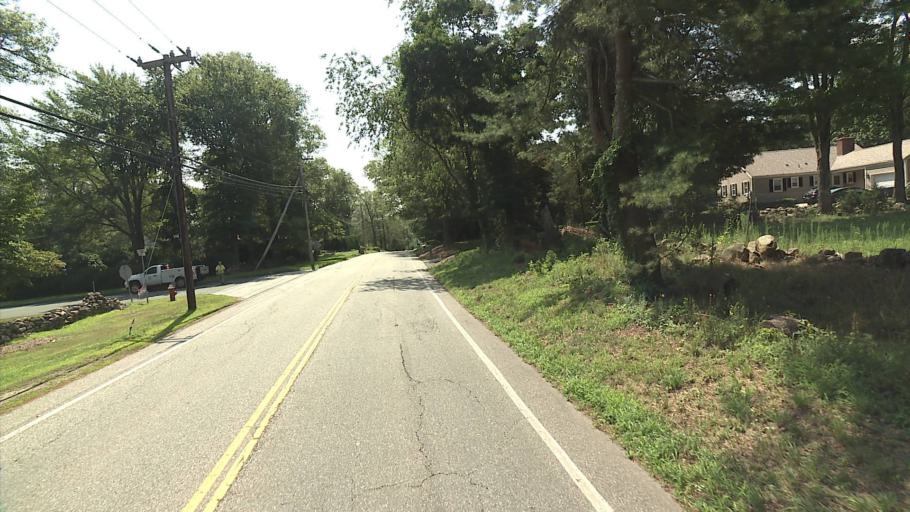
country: US
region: Connecticut
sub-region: New London County
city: Niantic
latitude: 41.3767
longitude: -72.2132
